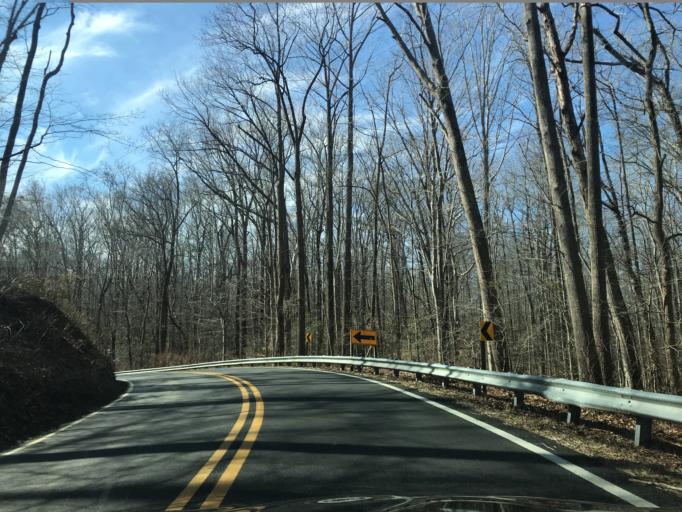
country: US
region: Maryland
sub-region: Charles County
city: Indian Head
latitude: 38.5040
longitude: -77.1562
